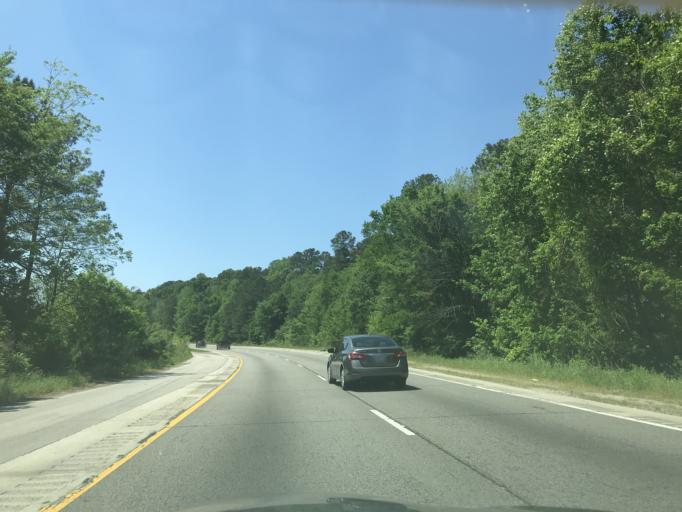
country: US
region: North Carolina
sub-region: Wake County
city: Garner
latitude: 35.7546
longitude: -78.5901
